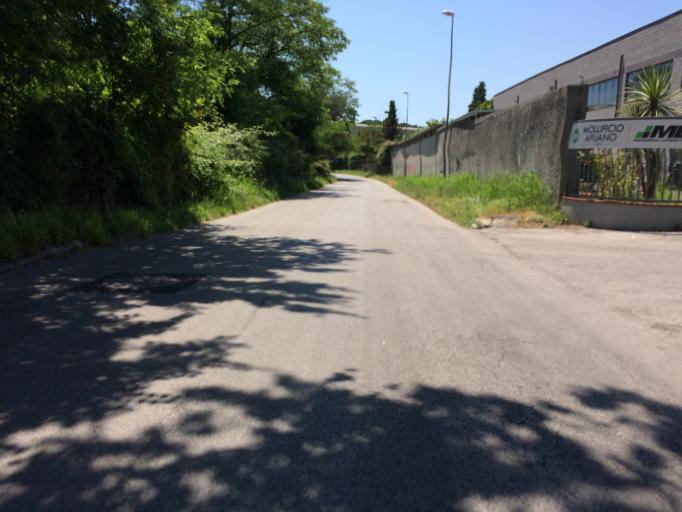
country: IT
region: Tuscany
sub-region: Provincia di Massa-Carrara
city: Massa
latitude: 44.0352
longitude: 10.1237
